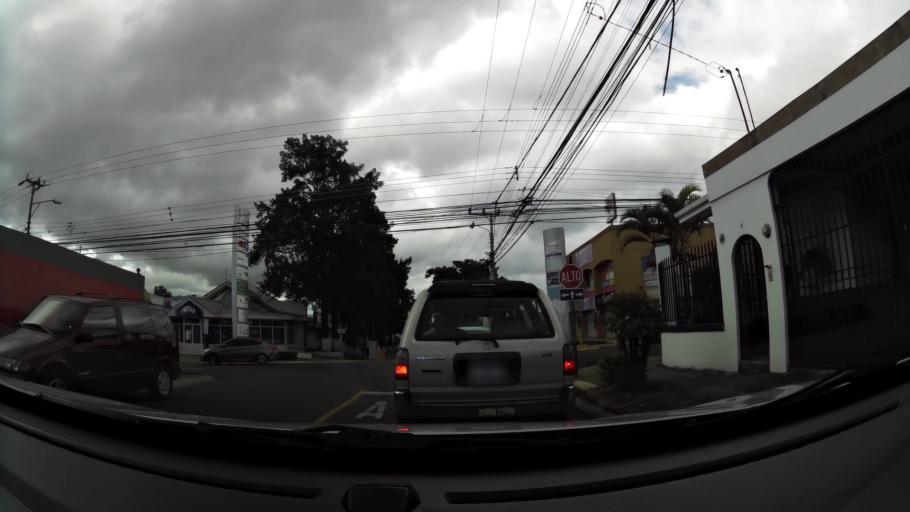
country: CR
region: San Jose
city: San Pedro
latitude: 9.9218
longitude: -84.0430
